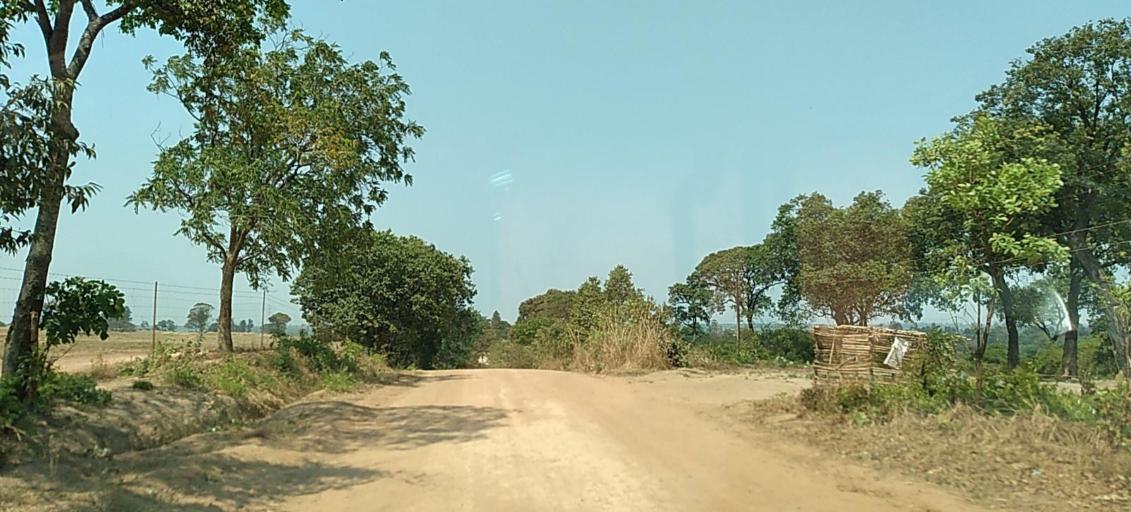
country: ZM
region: Copperbelt
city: Chambishi
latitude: -12.6221
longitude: 27.9537
